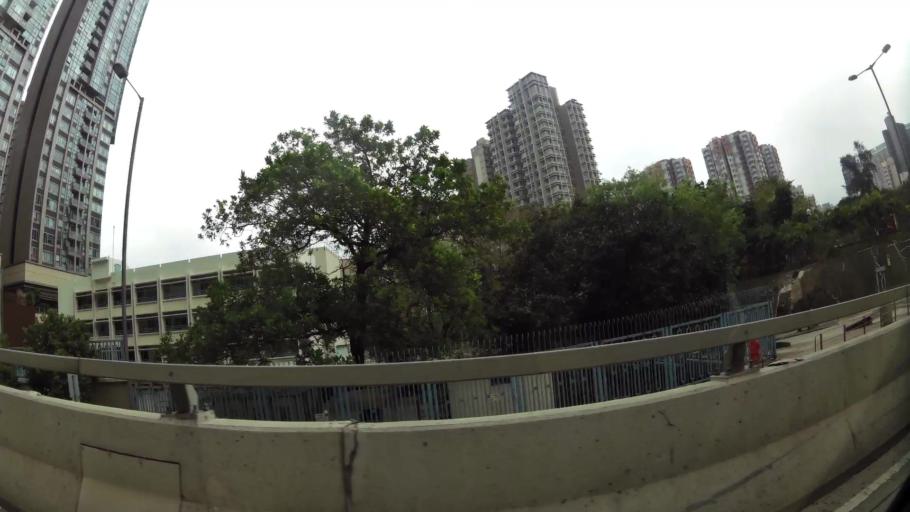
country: HK
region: Kowloon City
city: Kowloon
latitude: 22.3107
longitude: 114.1854
